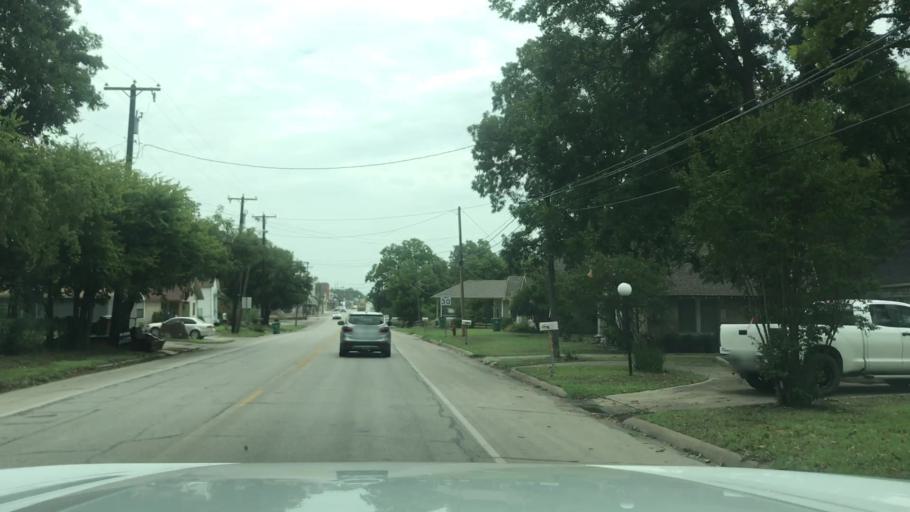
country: US
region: Texas
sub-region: Erath County
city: Dublin
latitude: 32.0859
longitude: -98.3455
